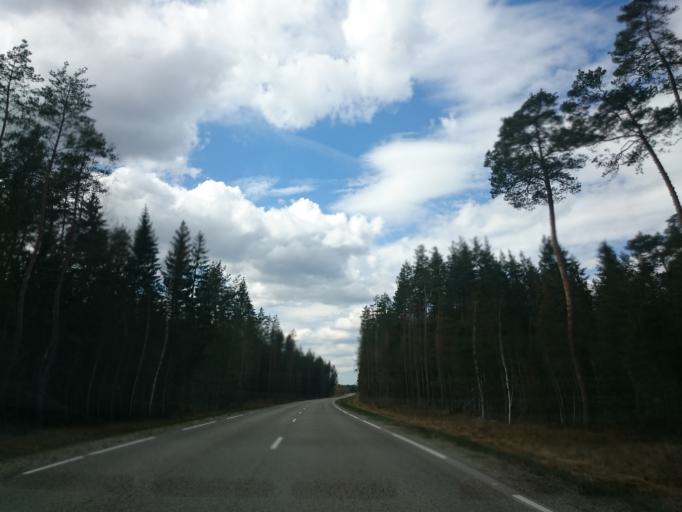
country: LV
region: Kuldigas Rajons
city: Kuldiga
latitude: 56.9507
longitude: 22.2585
